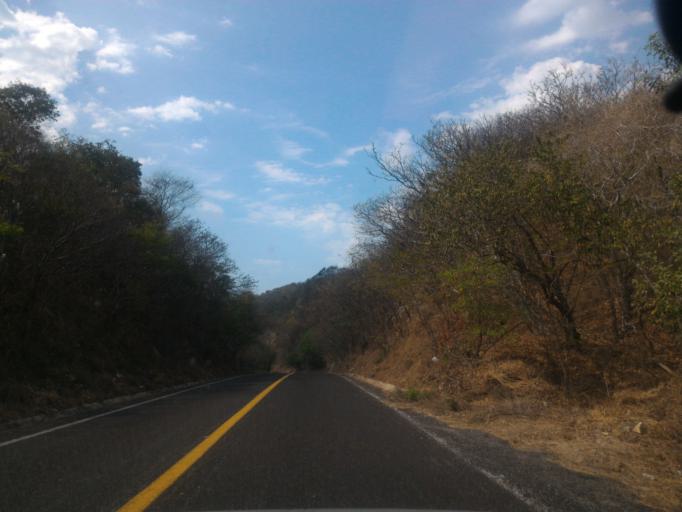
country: MX
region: Michoacan
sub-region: Coalcoman de Vazquez Pallares
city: Coalcoman de Vazquez Pallares
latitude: 18.2814
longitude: -103.3758
